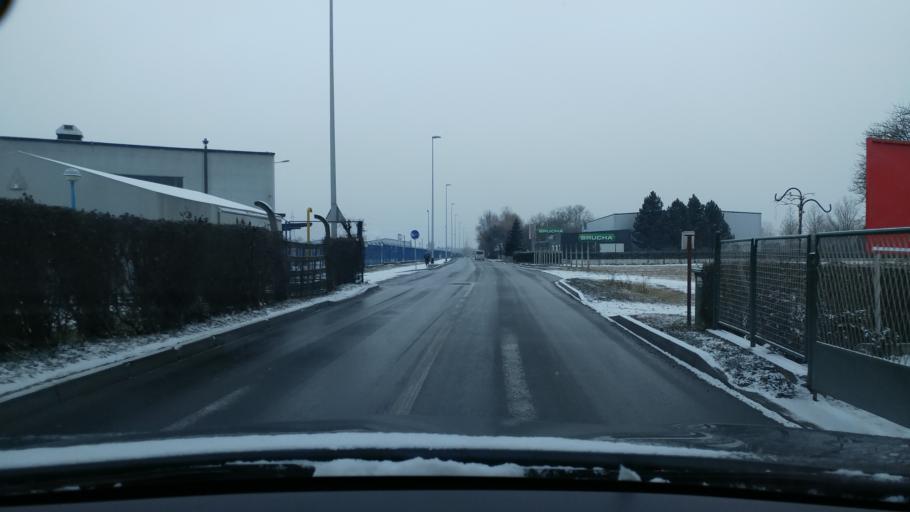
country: HR
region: Grad Zagreb
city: Stenjevec
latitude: 45.8028
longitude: 15.8747
